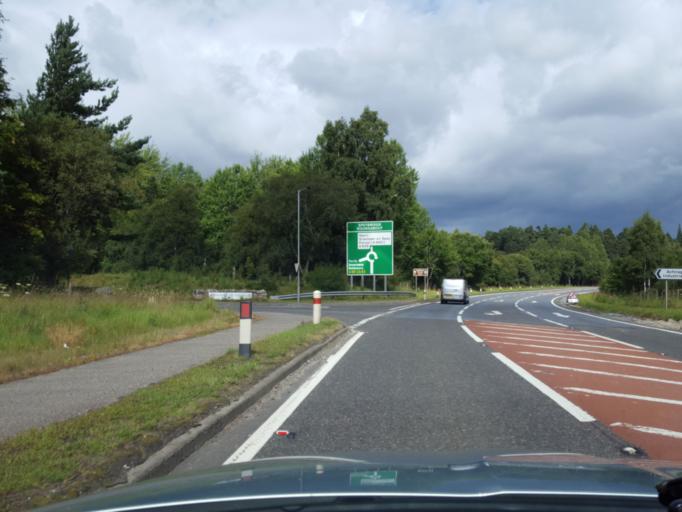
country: GB
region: Scotland
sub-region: Highland
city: Grantown on Spey
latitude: 57.3189
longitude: -3.6045
